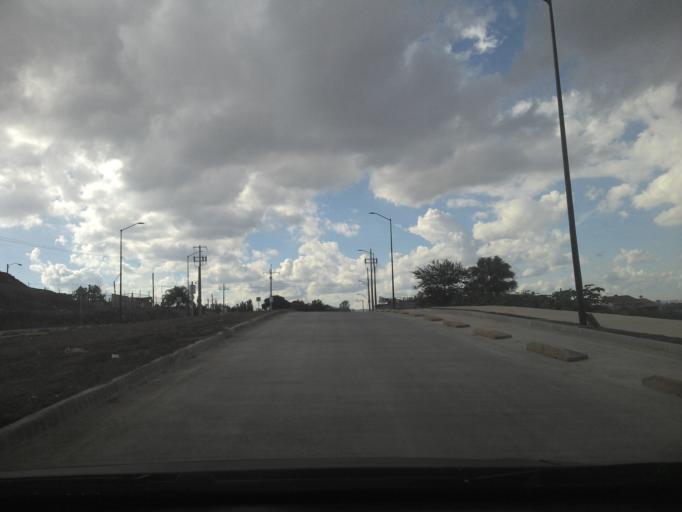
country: MX
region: Jalisco
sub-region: Tlajomulco de Zuniga
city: Altus Bosques
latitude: 20.6156
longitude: -103.3665
